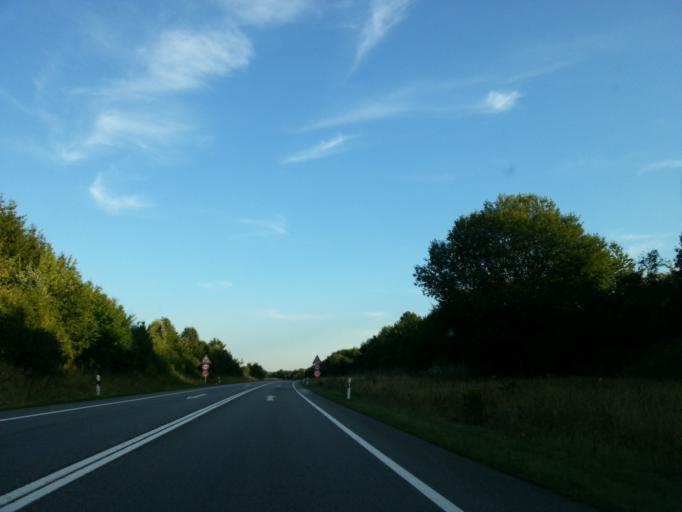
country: DE
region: Rheinland-Pfalz
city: Bann
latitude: 49.3830
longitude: 7.6050
